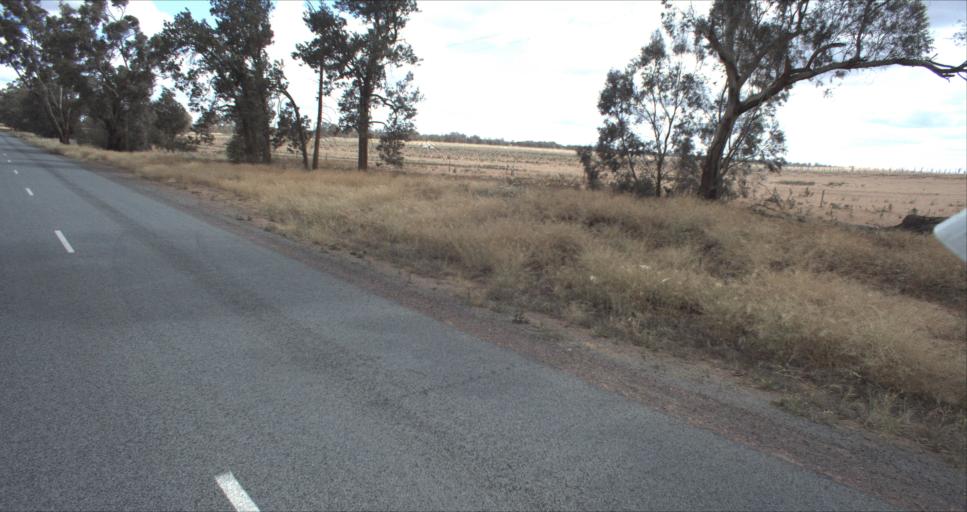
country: AU
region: New South Wales
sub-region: Leeton
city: Leeton
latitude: -34.6605
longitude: 146.3494
